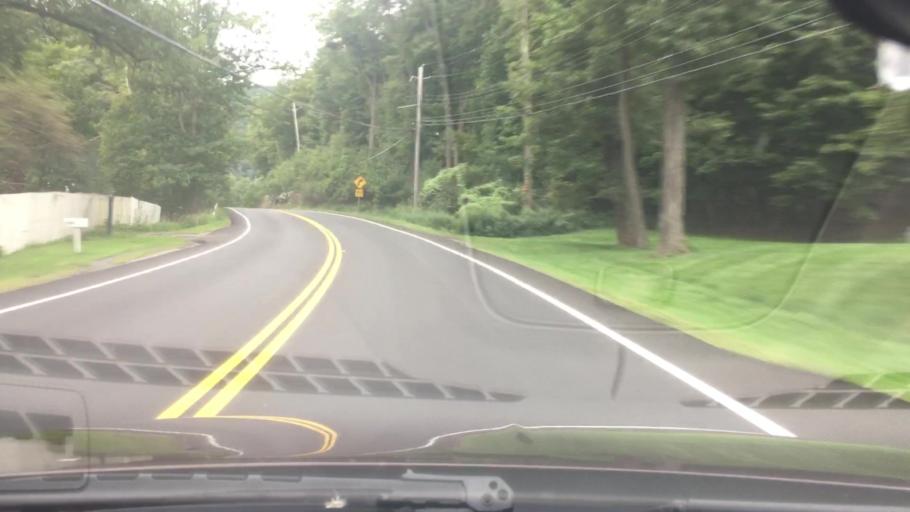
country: US
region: New York
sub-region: Dutchess County
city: Dover Plains
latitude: 41.8460
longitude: -73.5862
